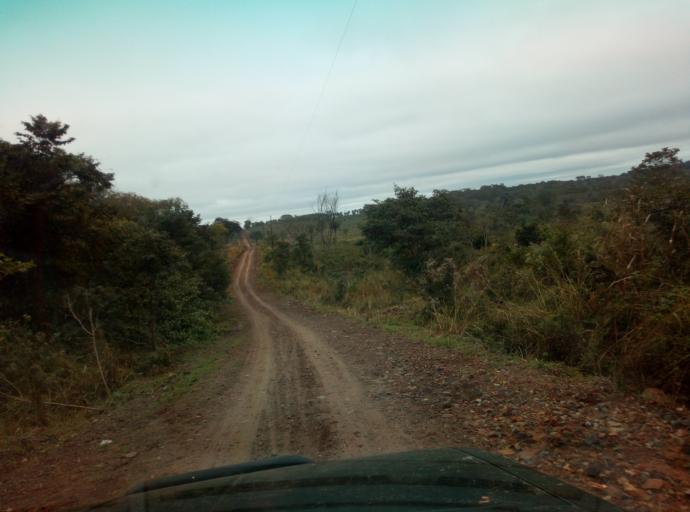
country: PY
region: Caaguazu
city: Carayao
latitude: -25.1903
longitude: -56.3685
